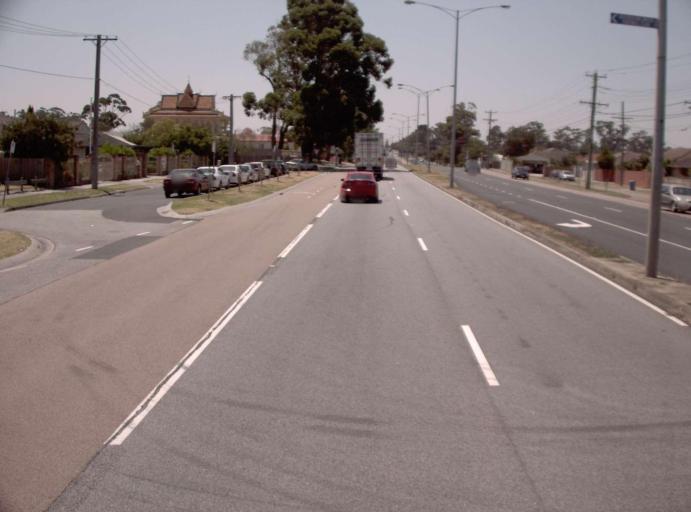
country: AU
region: Victoria
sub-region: Greater Dandenong
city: Springvale South
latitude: -37.9702
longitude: 145.1486
